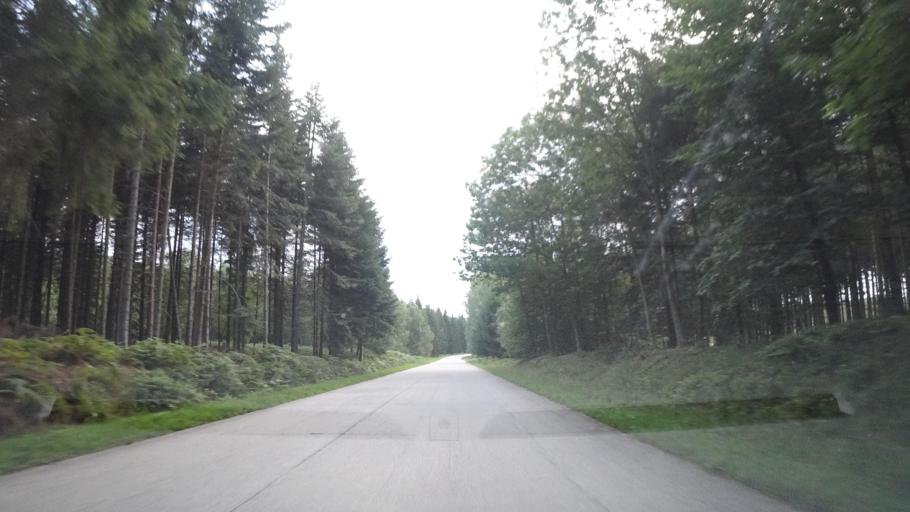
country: BE
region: Wallonia
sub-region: Province du Luxembourg
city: Herbeumont
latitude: 49.8004
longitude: 5.2593
